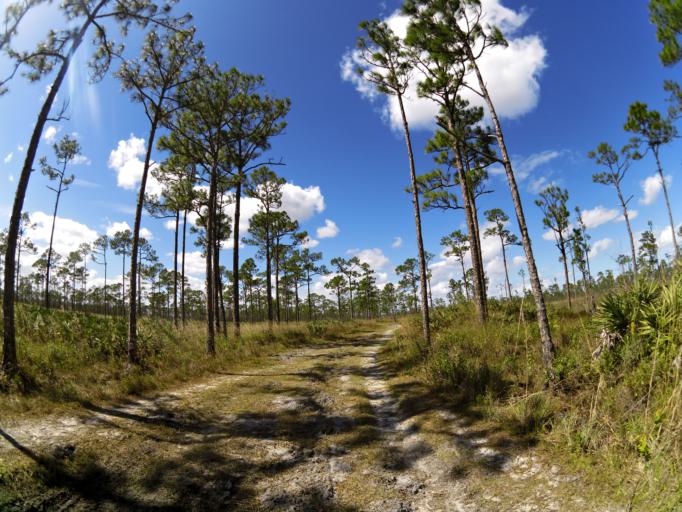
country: US
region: Florida
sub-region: Martin County
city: Hobe Sound
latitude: 27.0171
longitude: -80.1435
